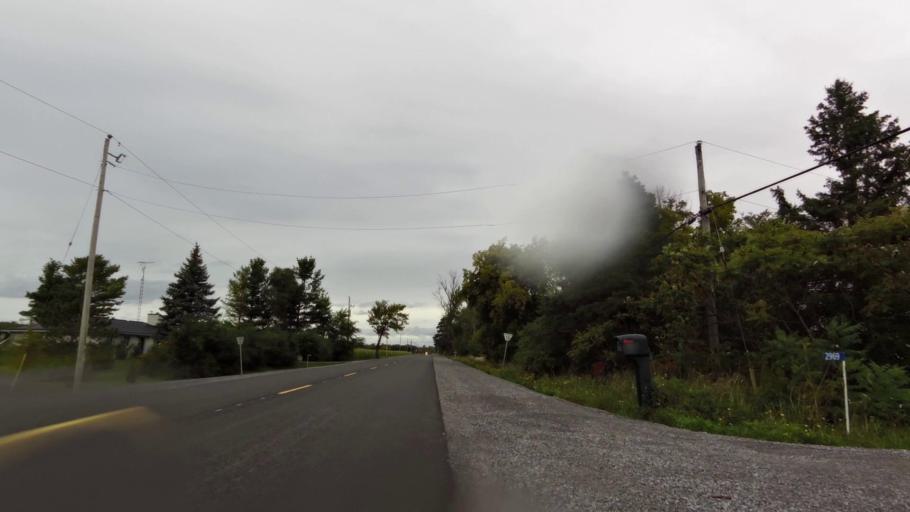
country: CA
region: Ontario
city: Bells Corners
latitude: 45.1476
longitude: -75.6341
